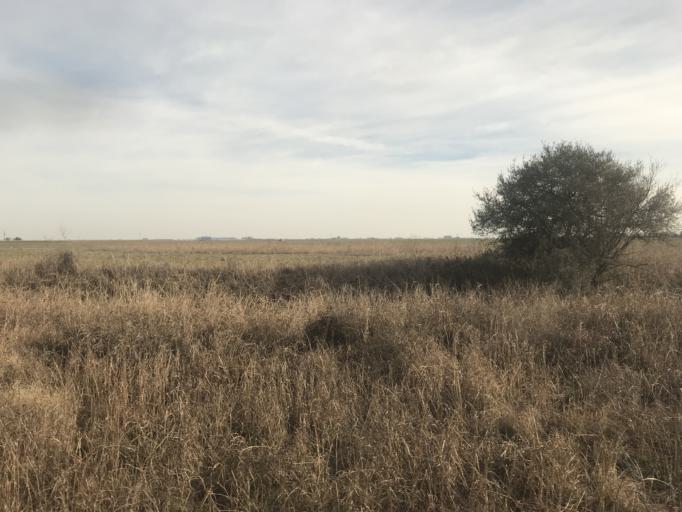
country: AR
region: Cordoba
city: Pilar
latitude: -31.6944
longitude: -63.8751
